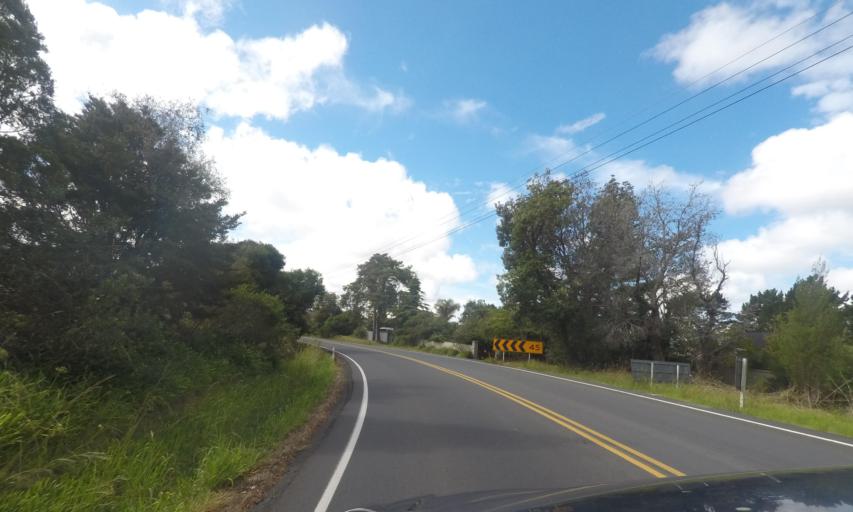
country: NZ
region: Auckland
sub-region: Auckland
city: Rosebank
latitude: -36.7974
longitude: 174.6360
